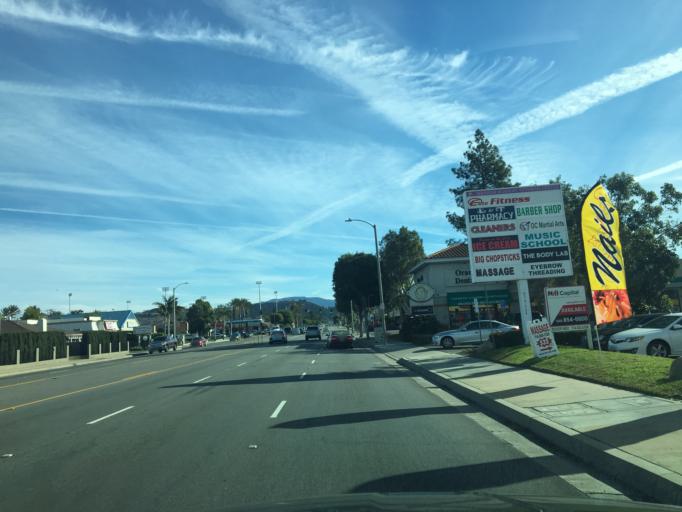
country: US
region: California
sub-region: Orange County
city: Villa Park
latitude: 33.7877
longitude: -117.8204
